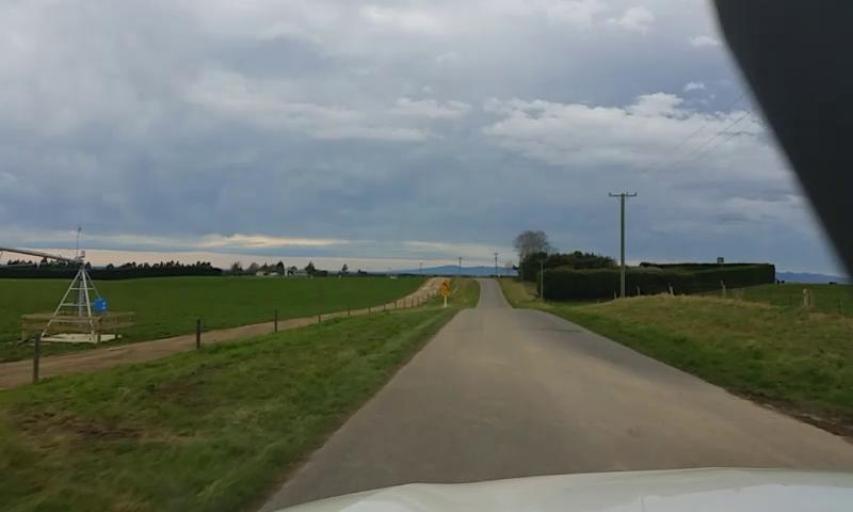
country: NZ
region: Canterbury
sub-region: Waimakariri District
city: Kaiapoi
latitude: -43.2950
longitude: 172.4745
